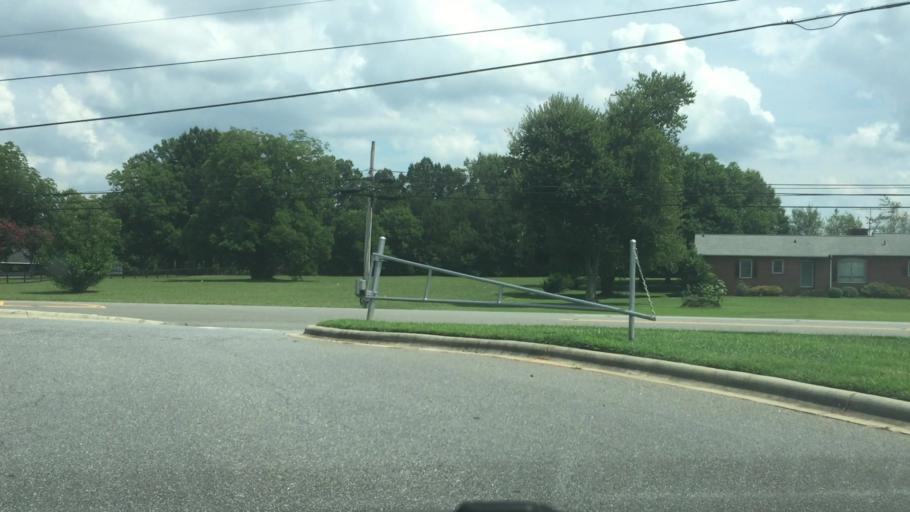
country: US
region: North Carolina
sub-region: Iredell County
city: Mooresville
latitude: 35.5957
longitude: -80.7841
